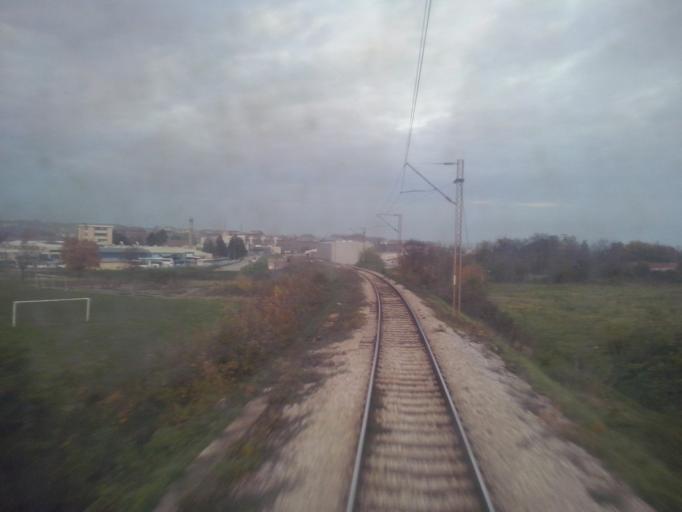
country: RS
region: Central Serbia
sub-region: Kolubarski Okrug
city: Valjevo
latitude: 44.2650
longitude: 19.8938
